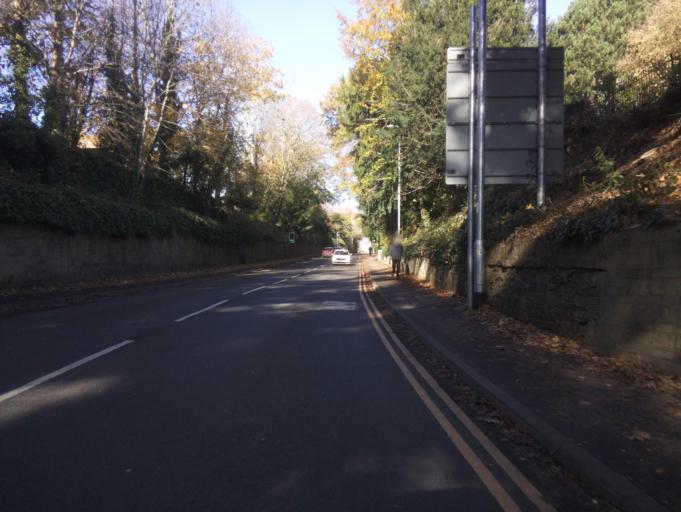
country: GB
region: England
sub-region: Somerset
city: Yeovil
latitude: 50.9472
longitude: -2.6383
